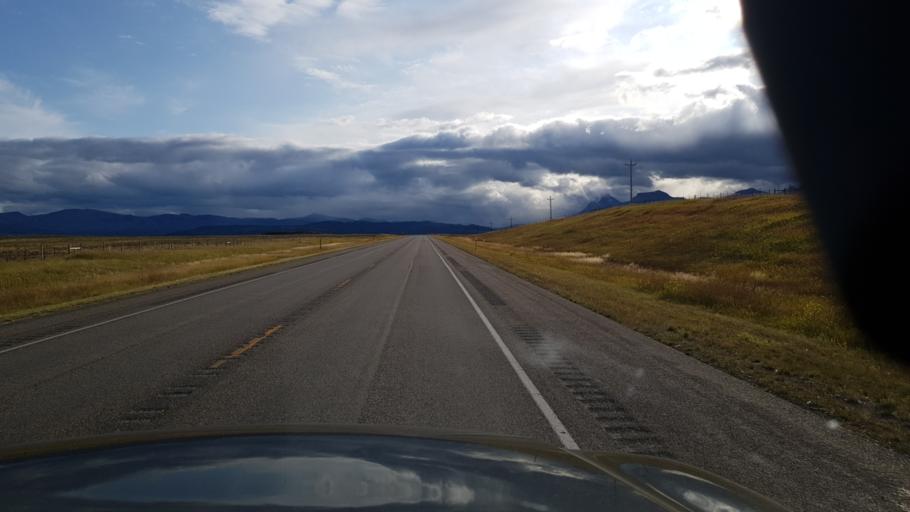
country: US
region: Montana
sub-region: Glacier County
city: South Browning
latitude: 48.4745
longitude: -113.1460
